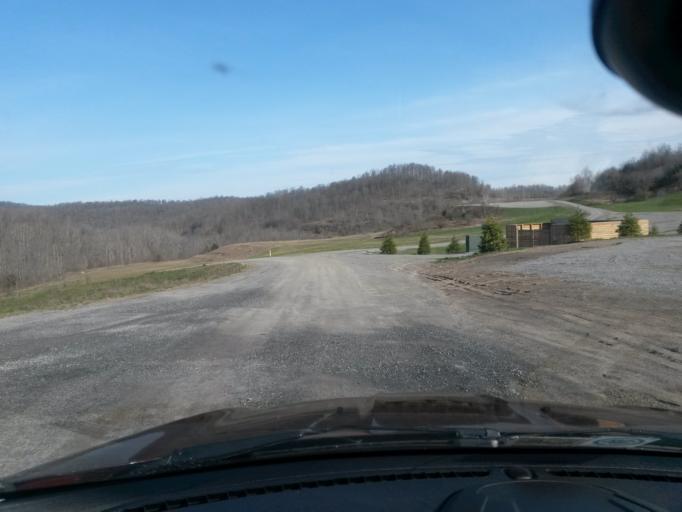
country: US
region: West Virginia
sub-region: Fayette County
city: Mount Hope
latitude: 37.9078
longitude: -81.1724
